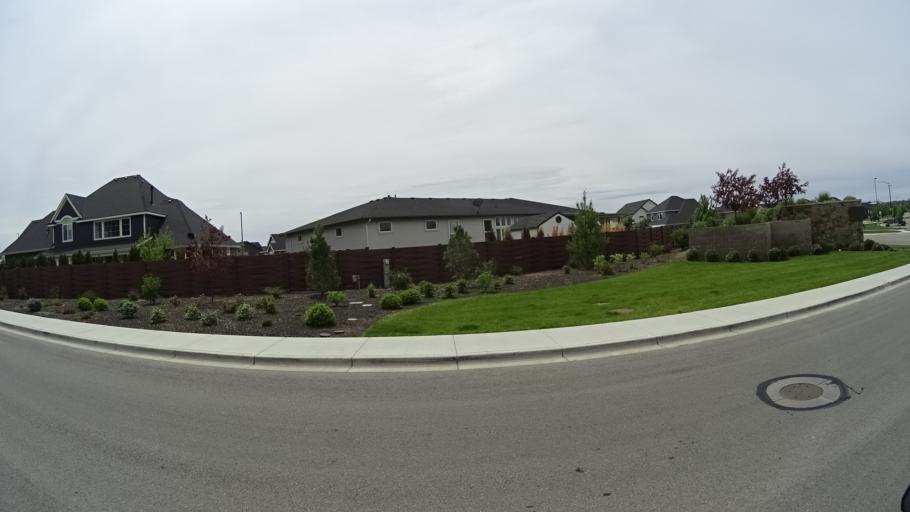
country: US
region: Idaho
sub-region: Ada County
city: Meridian
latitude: 43.5575
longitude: -116.3439
